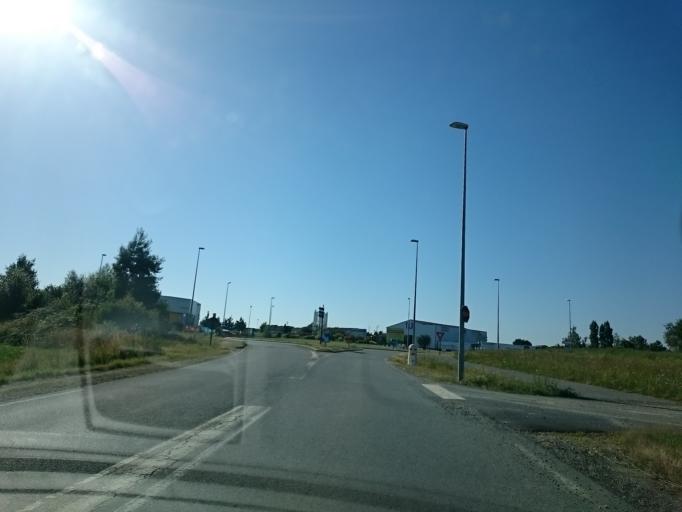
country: FR
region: Brittany
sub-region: Departement d'Ille-et-Vilaine
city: Corps-Nuds
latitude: 47.9888
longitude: -1.5909
